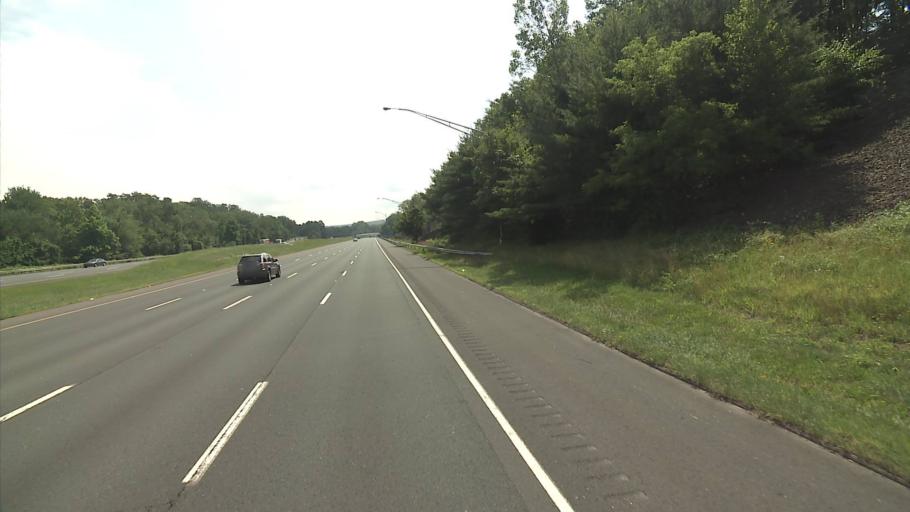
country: US
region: Connecticut
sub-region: Hartford County
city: Manchester
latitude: 41.7625
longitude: -72.5283
